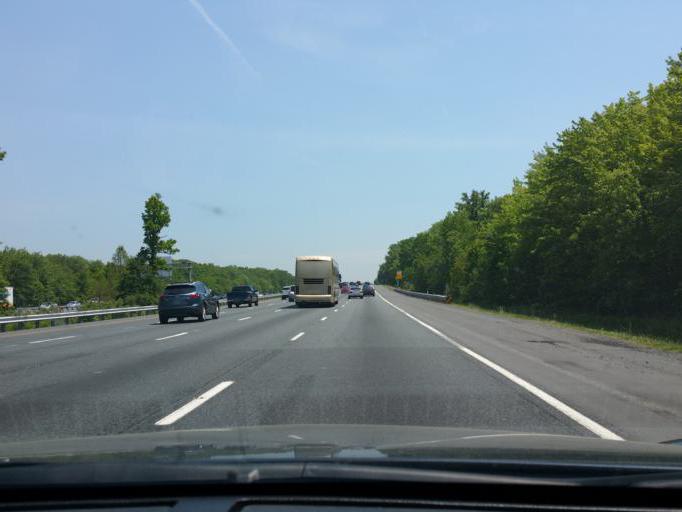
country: US
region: Maryland
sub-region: Baltimore County
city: White Marsh
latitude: 39.4027
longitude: -76.4236
